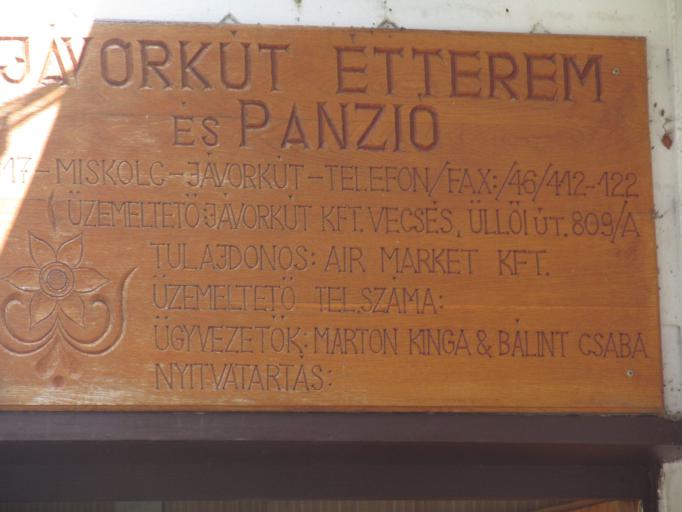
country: HU
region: Heves
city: Szilvasvarad
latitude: 48.0973
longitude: 20.5246
